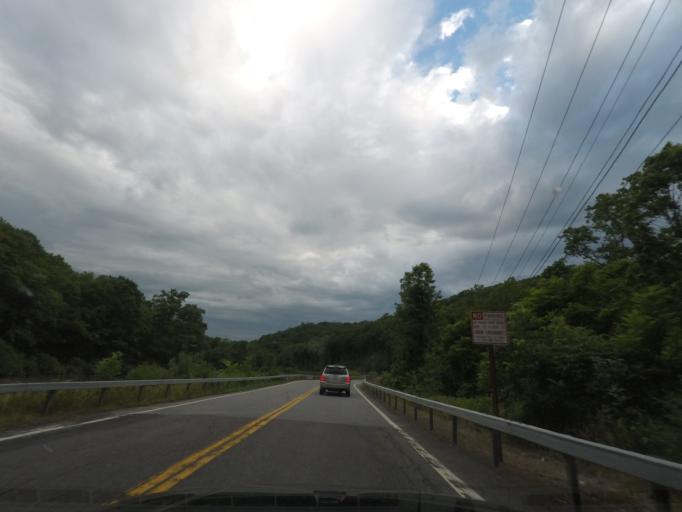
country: US
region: New York
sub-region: Dutchess County
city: Pine Plains
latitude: 41.9739
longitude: -73.7337
